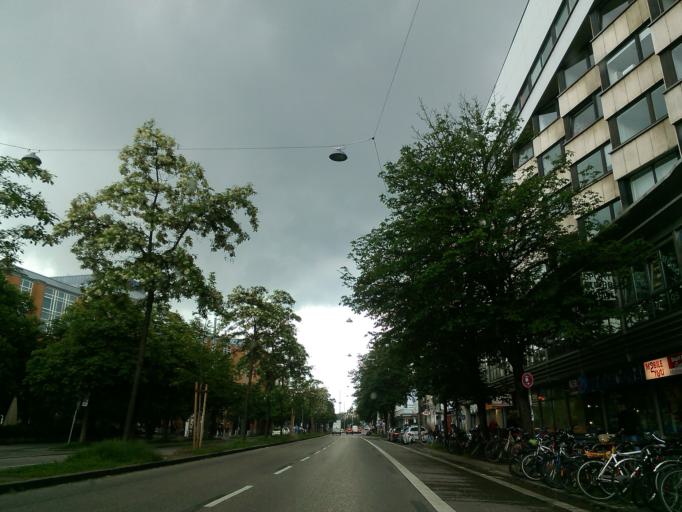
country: DE
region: Bavaria
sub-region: Upper Bavaria
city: Munich
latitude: 48.1302
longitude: 11.5914
